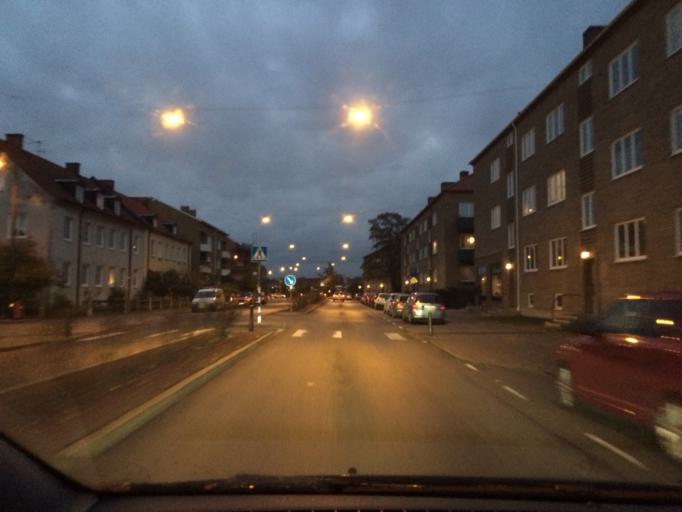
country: SE
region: Skane
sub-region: Malmo
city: Bunkeflostrand
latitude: 55.5810
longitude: 12.9388
